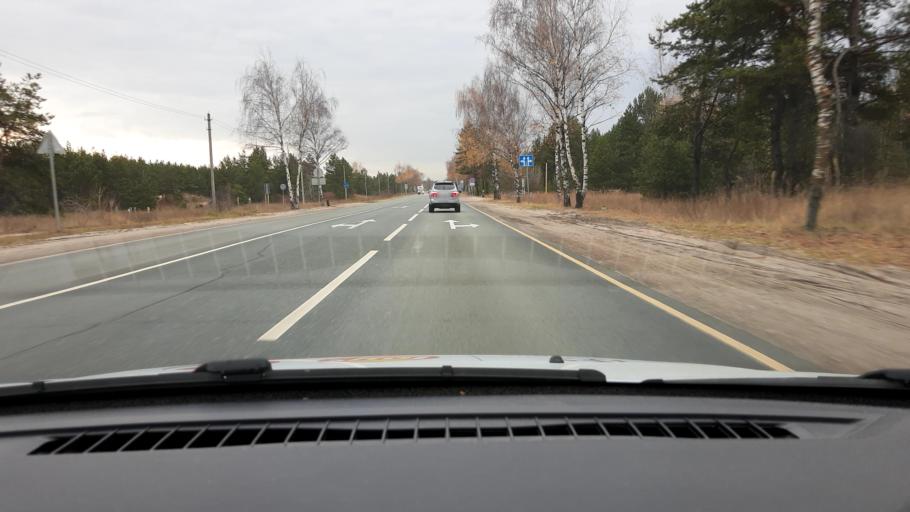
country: RU
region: Nizjnij Novgorod
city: Dzerzhinsk
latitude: 56.2851
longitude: 43.4756
